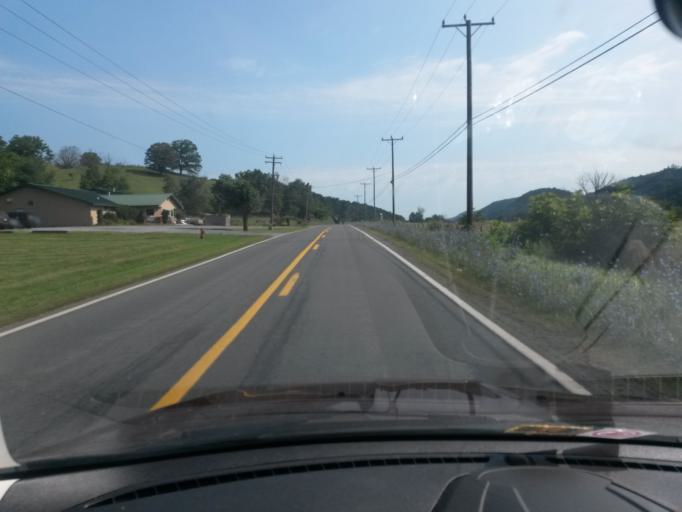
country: US
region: Virginia
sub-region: Shenandoah County
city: Basye
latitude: 38.9877
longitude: -78.7826
